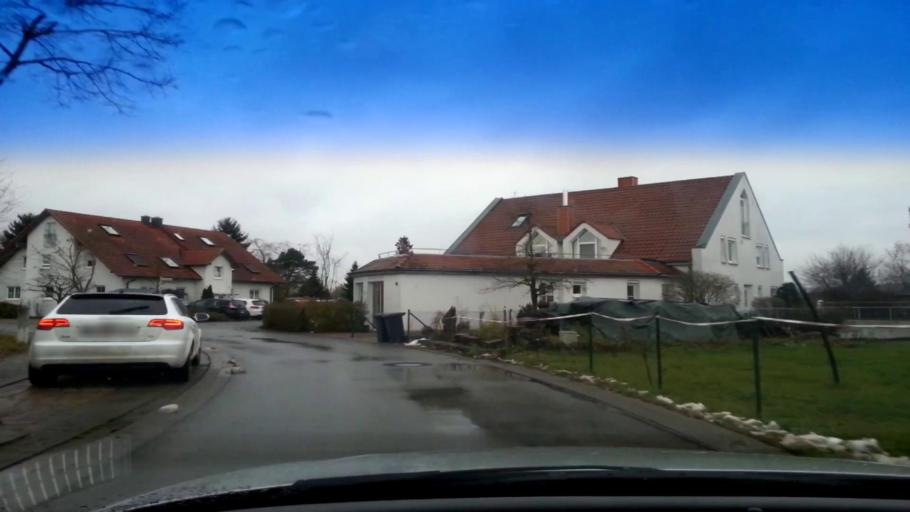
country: DE
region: Bavaria
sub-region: Upper Franconia
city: Gundelsheim
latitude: 49.9269
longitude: 10.9286
